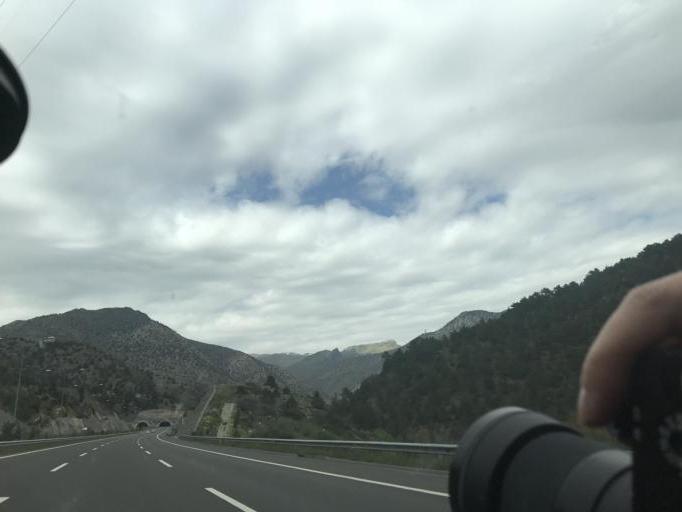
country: TR
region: Nigde
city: Ciftehan
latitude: 37.5140
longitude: 34.8178
